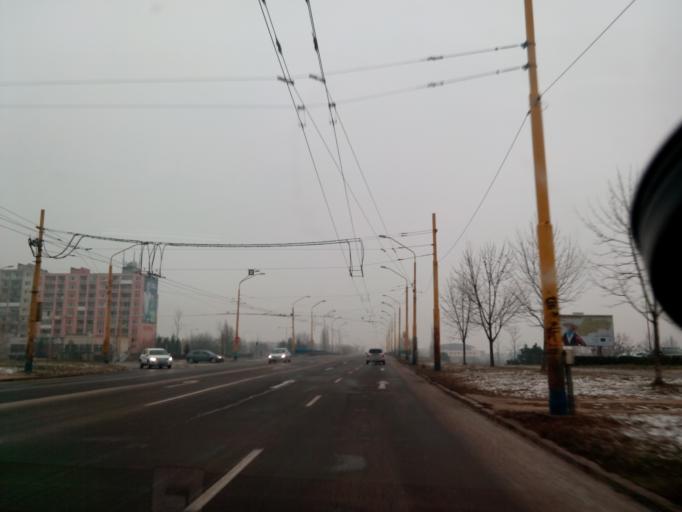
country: SK
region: Kosicky
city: Kosice
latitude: 48.7118
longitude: 21.2141
